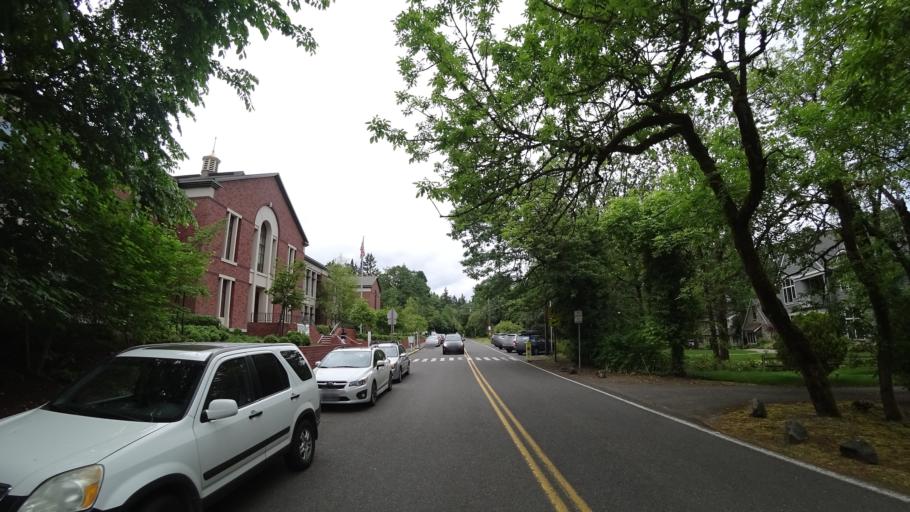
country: US
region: Oregon
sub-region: Clackamas County
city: Milwaukie
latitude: 45.4398
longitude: -122.6556
